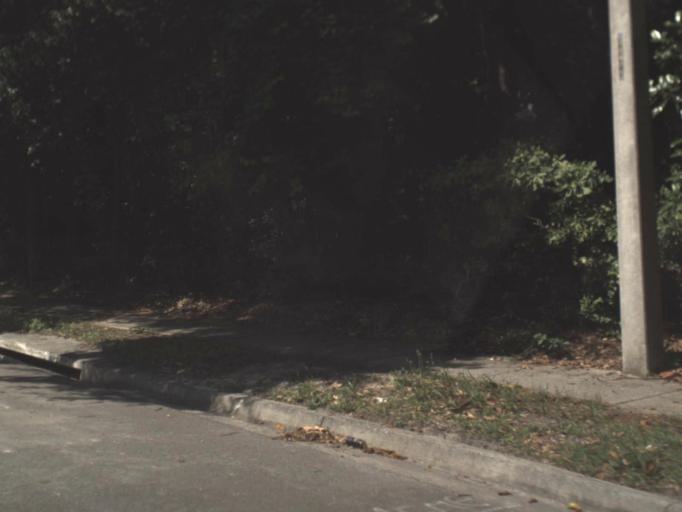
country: US
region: Florida
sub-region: Duval County
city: Jacksonville
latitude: 30.4430
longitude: -81.7006
